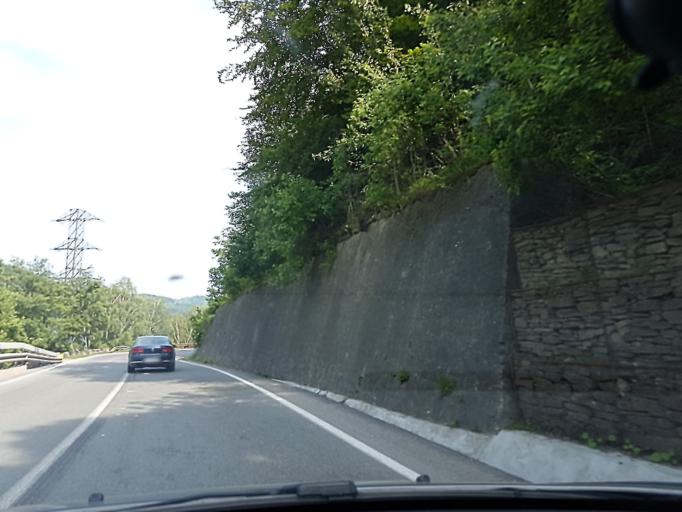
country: RO
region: Prahova
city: Maneciu
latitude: 45.3375
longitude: 25.9614
